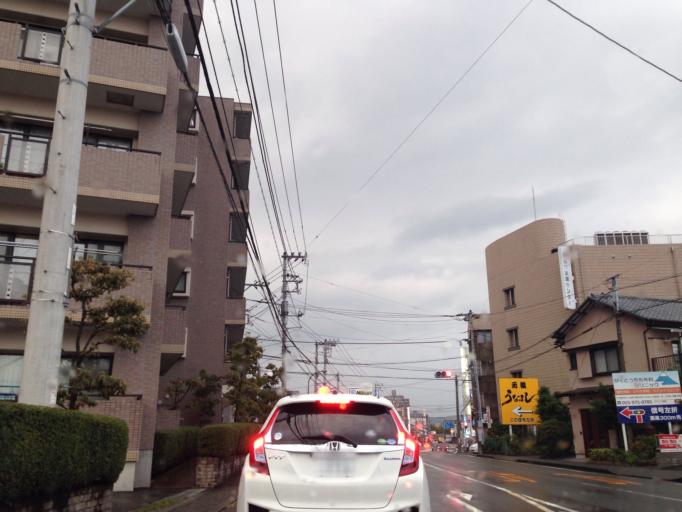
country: JP
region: Shizuoka
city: Mishima
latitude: 35.1117
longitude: 138.9148
